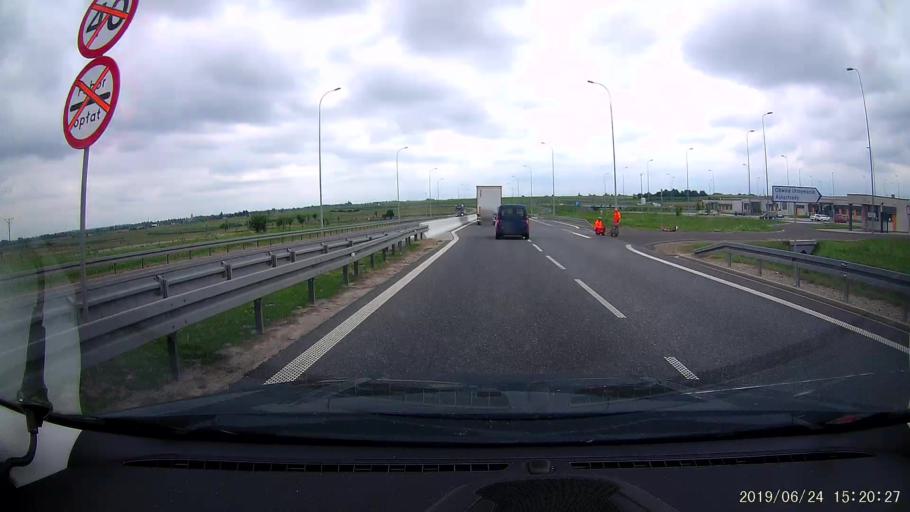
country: PL
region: Subcarpathian Voivodeship
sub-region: Powiat przeworski
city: Mirocin
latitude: 50.0415
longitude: 22.5760
